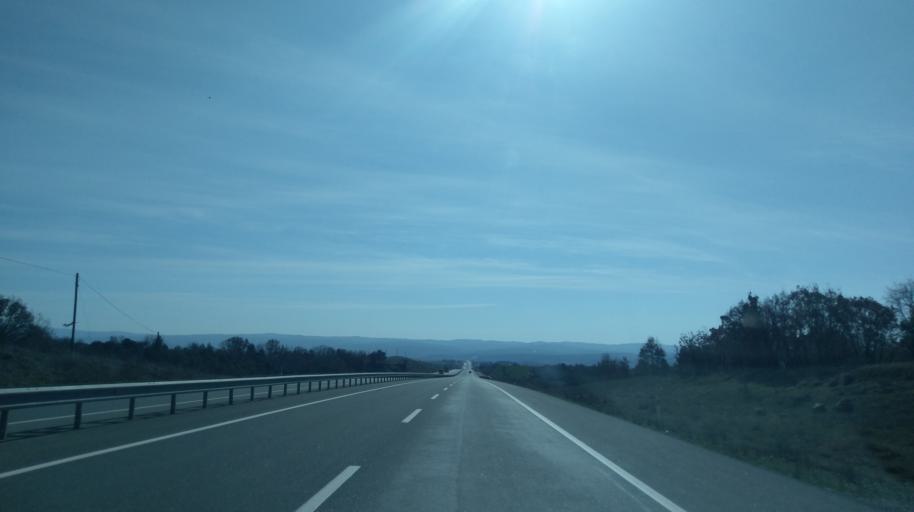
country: TR
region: Edirne
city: Kesan
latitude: 40.8038
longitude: 26.6633
